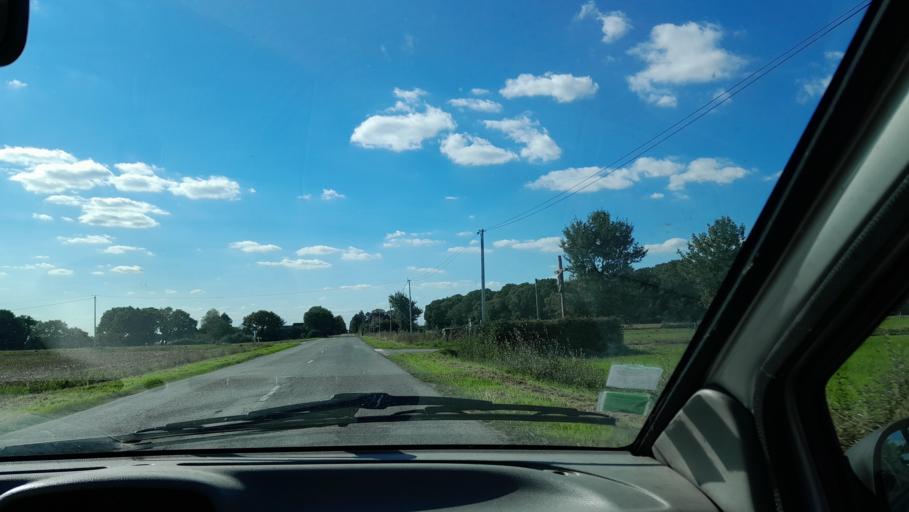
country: FR
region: Brittany
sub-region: Departement d'Ille-et-Vilaine
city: Le Pertre
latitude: 47.9694
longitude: -1.0988
